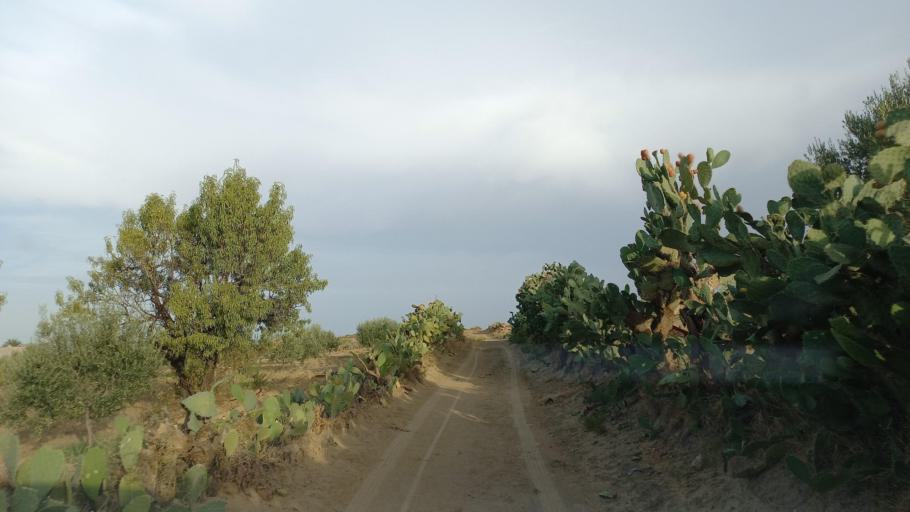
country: TN
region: Al Qasrayn
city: Kasserine
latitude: 35.2169
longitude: 9.0557
